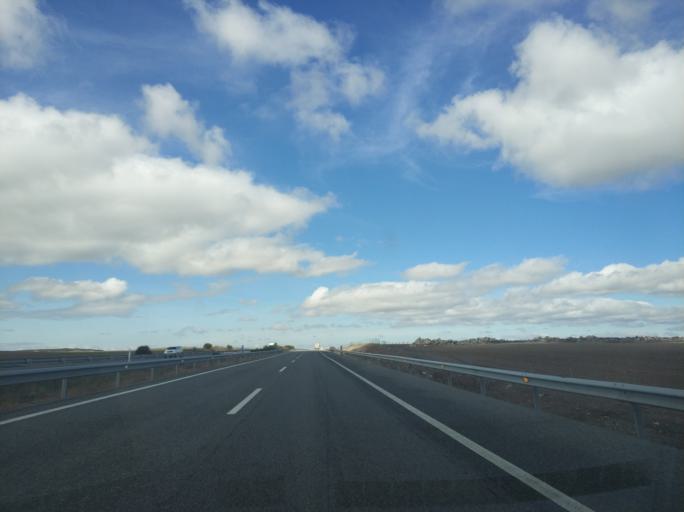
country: ES
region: Castille and Leon
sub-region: Provincia de Burgos
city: Albillos
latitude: 42.3045
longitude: -3.7723
